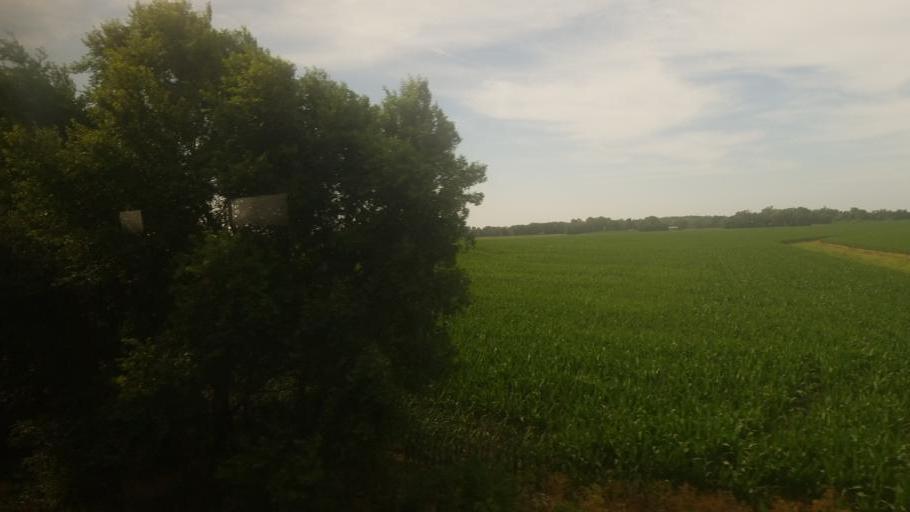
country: US
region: Kansas
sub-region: Douglas County
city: Eudora
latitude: 38.9498
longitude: -95.1356
